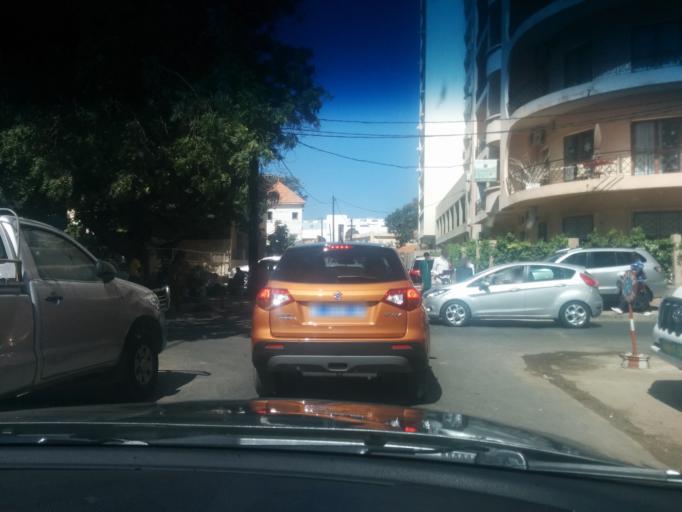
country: SN
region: Dakar
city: Dakar
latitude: 14.6680
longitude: -17.4405
